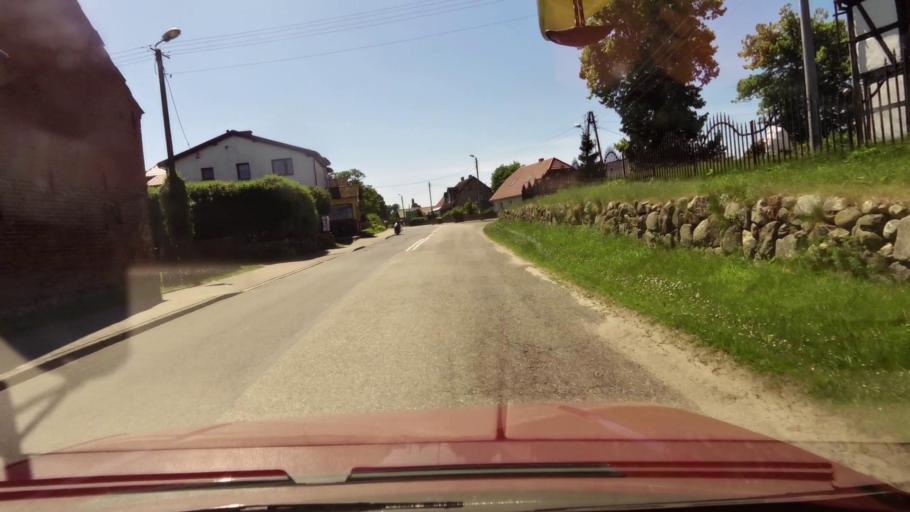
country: PL
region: West Pomeranian Voivodeship
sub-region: Powiat koszalinski
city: Bobolice
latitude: 53.9926
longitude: 16.6874
